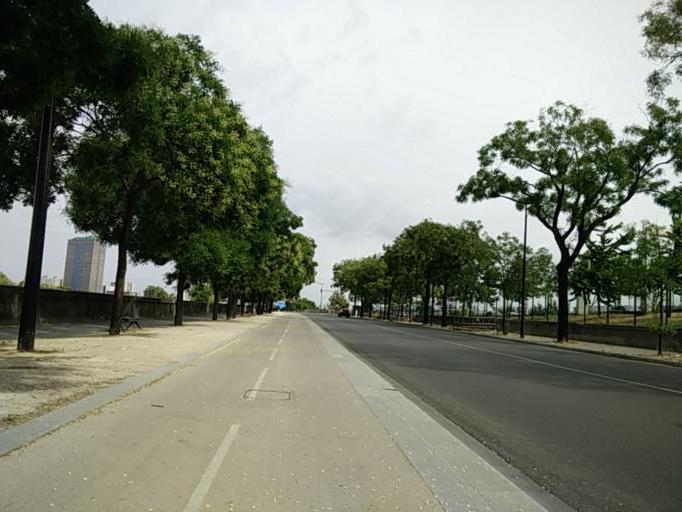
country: FR
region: Ile-de-France
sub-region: Departement de Seine-Saint-Denis
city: Le Pre-Saint-Gervais
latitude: 48.8940
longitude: 2.3944
